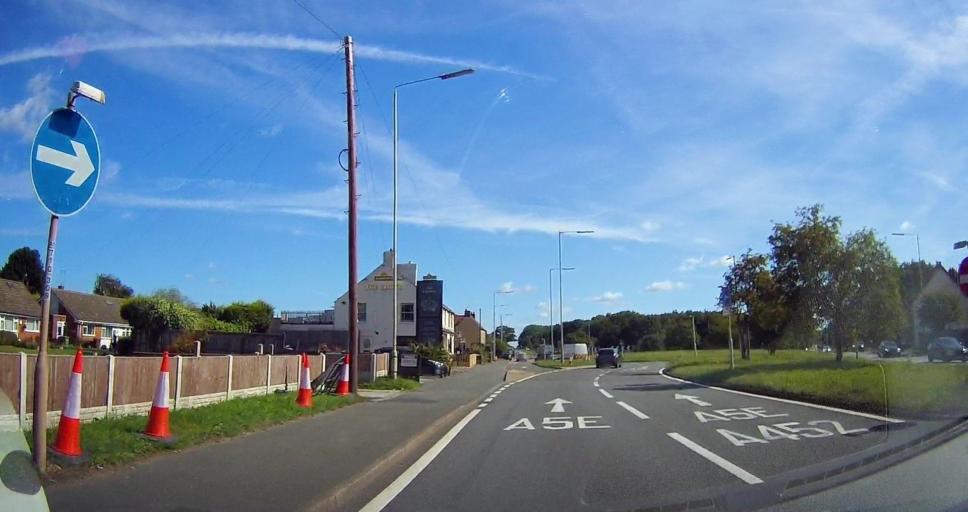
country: GB
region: England
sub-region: Staffordshire
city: Norton Canes
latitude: 52.6561
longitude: -1.9536
